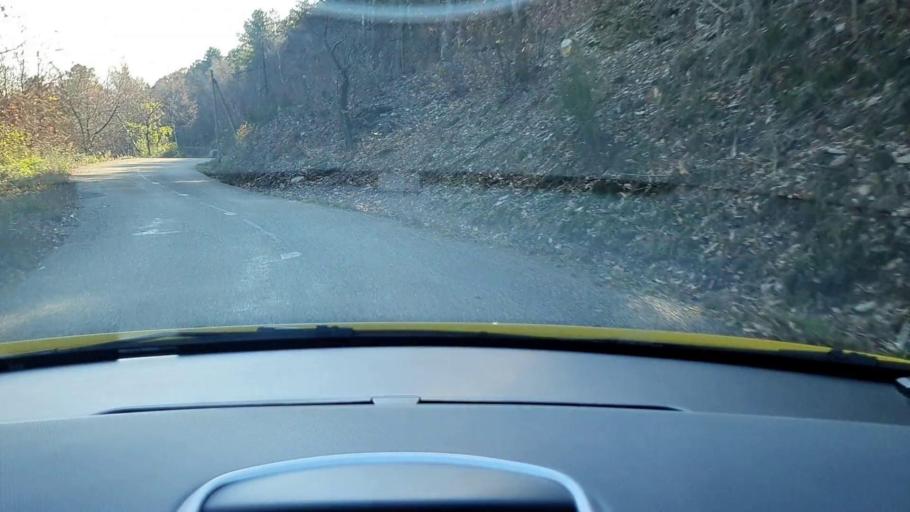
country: FR
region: Languedoc-Roussillon
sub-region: Departement du Gard
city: Branoux-les-Taillades
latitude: 44.2864
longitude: 3.9413
